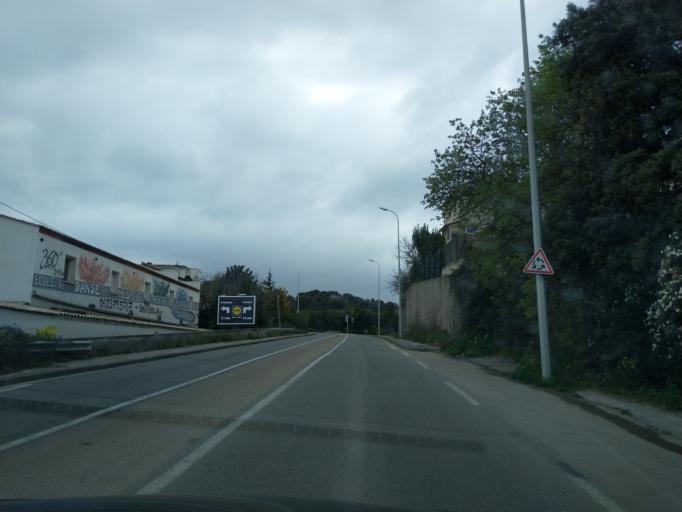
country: FR
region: Provence-Alpes-Cote d'Azur
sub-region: Departement des Bouches-du-Rhone
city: Allauch
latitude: 43.3182
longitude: 5.4691
